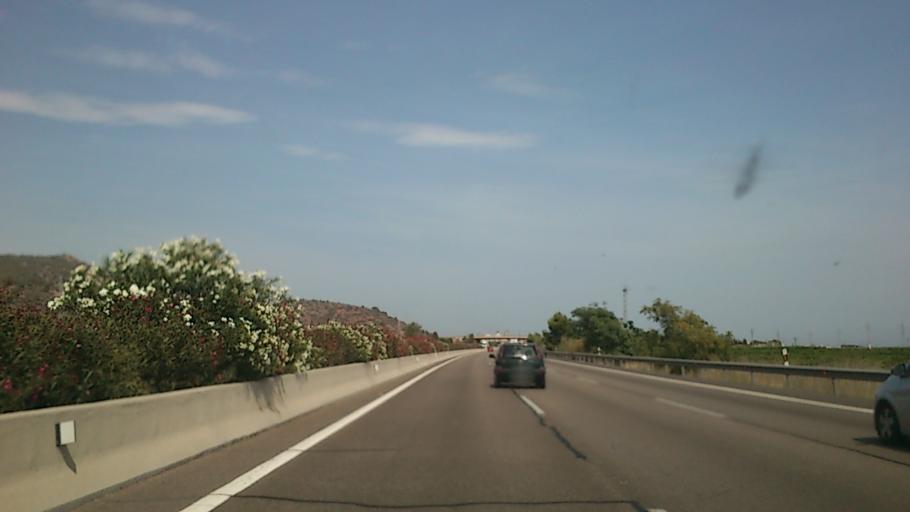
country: ES
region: Valencia
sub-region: Provincia de Valencia
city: Pucol
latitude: 39.6197
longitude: -0.3327
